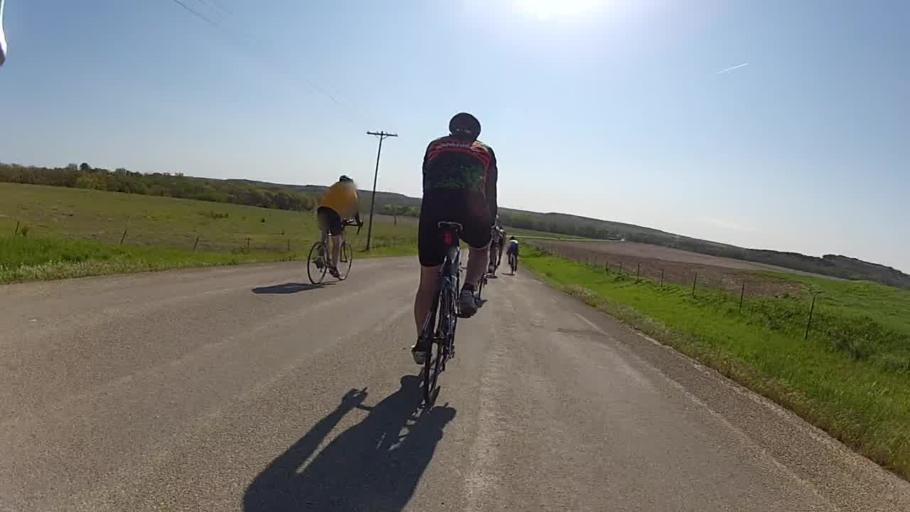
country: US
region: Kansas
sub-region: Geary County
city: Grandview Plaza
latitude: 39.0515
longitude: -96.7428
